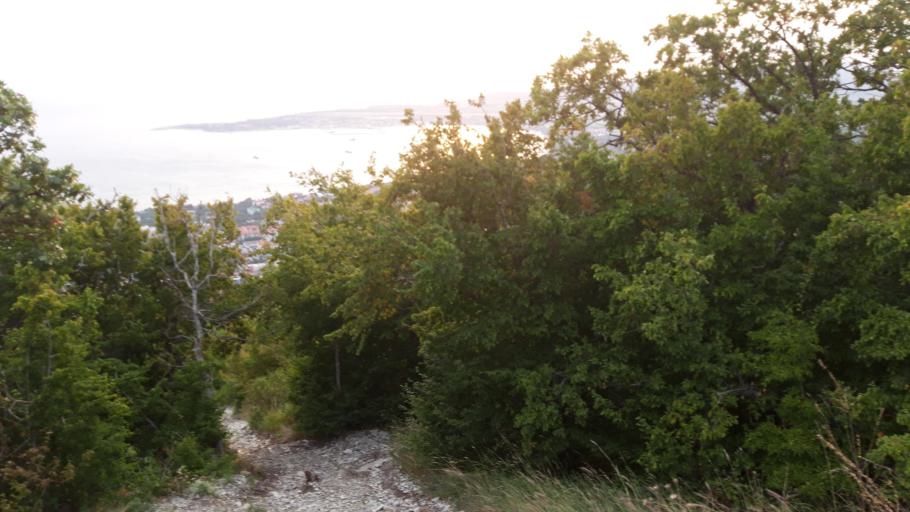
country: RU
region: Krasnodarskiy
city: Gelendzhik
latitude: 44.5844
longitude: 38.0921
